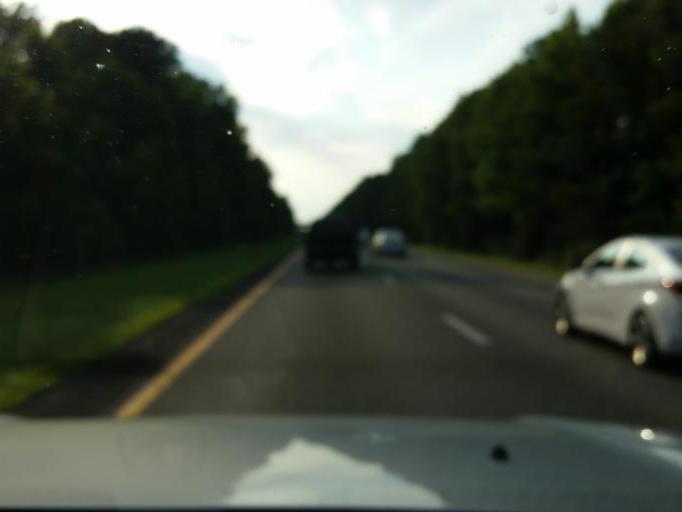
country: US
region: Virginia
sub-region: King William County
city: West Point
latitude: 37.4580
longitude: -76.8778
